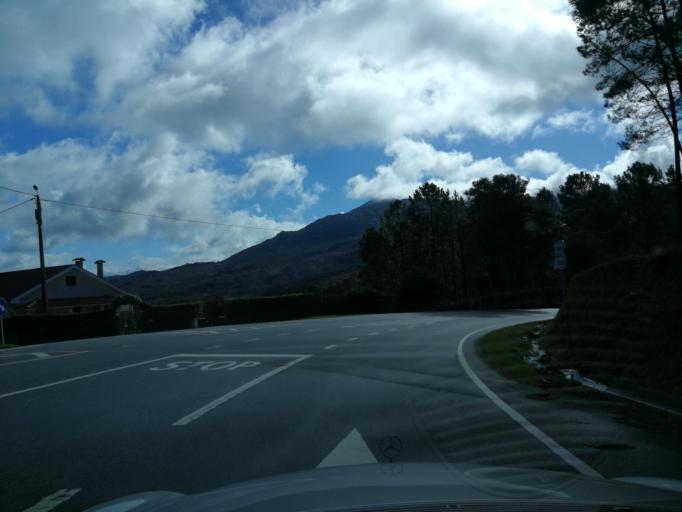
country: ES
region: Galicia
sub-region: Provincia de Ourense
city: Entrimo
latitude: 41.8716
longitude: -8.1932
